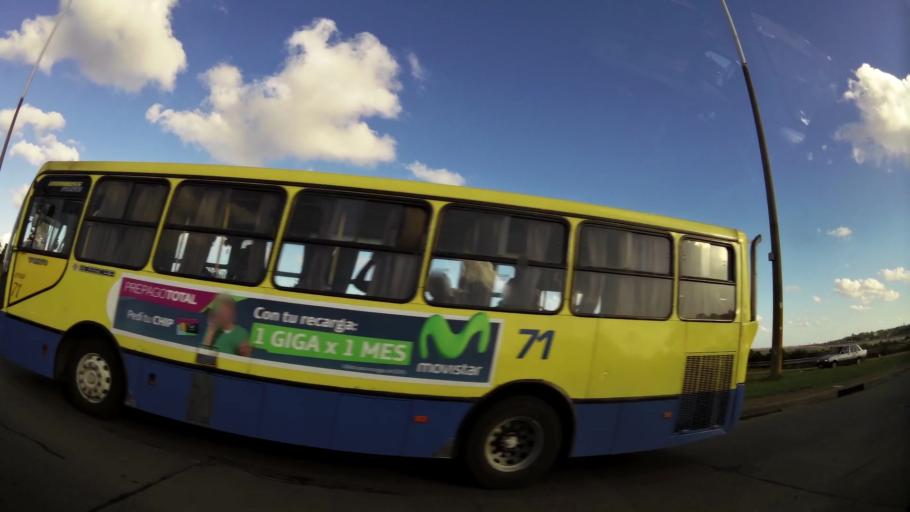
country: UY
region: Montevideo
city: Montevideo
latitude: -34.8722
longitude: -56.2432
